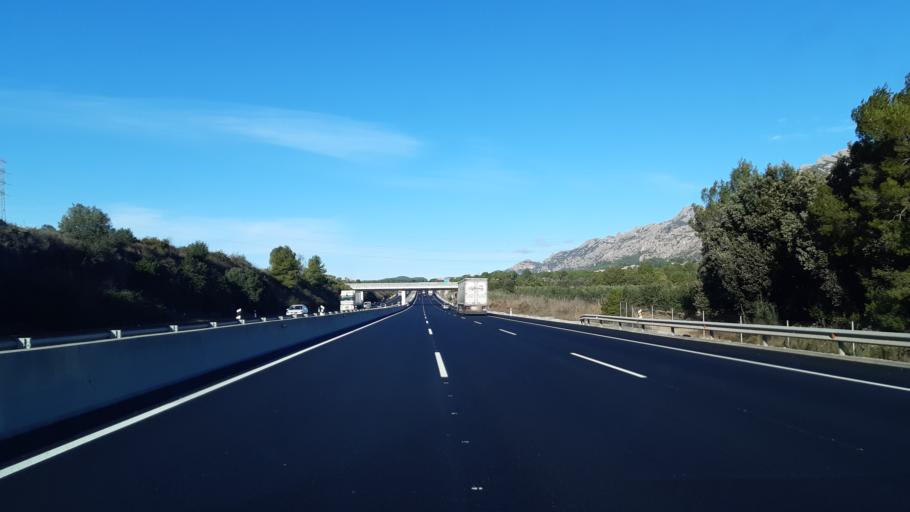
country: ES
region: Catalonia
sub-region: Provincia de Barcelona
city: Collbato
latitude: 41.5512
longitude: 1.8448
